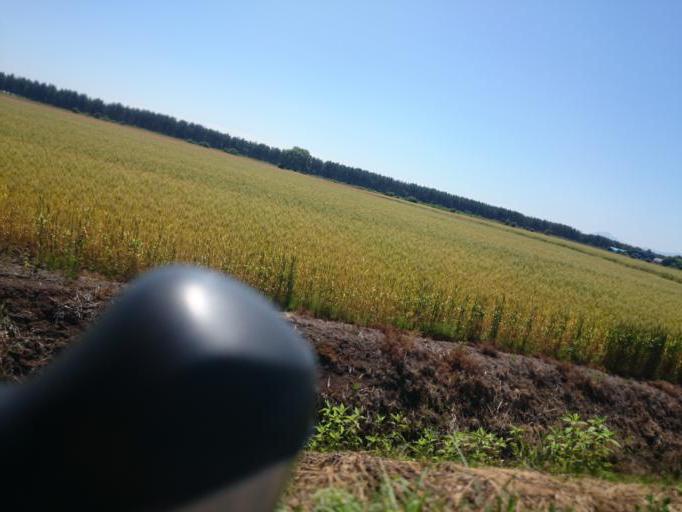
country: JP
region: Hokkaido
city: Ebetsu
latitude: 43.0740
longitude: 141.5768
